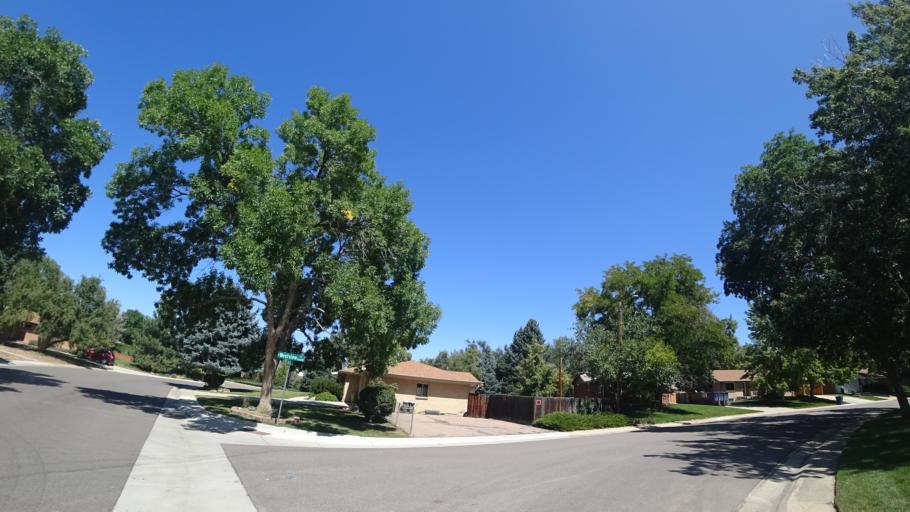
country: US
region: Colorado
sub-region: Arapahoe County
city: Littleton
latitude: 39.6072
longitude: -104.9922
